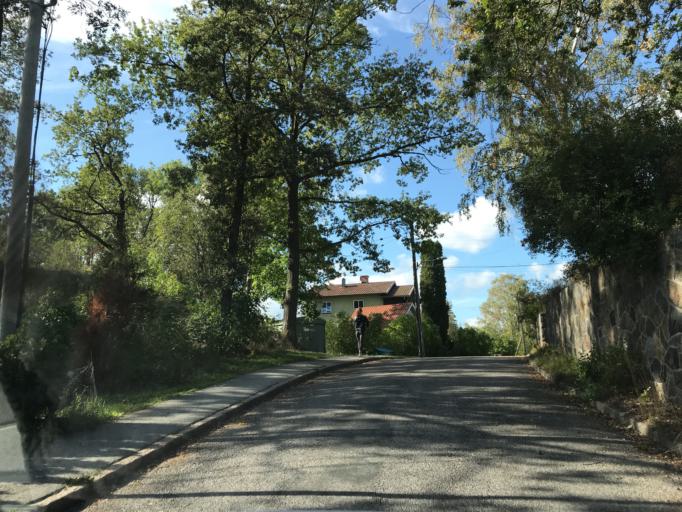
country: SE
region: Stockholm
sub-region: Huddinge Kommun
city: Segeltorp
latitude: 59.2753
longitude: 17.9682
